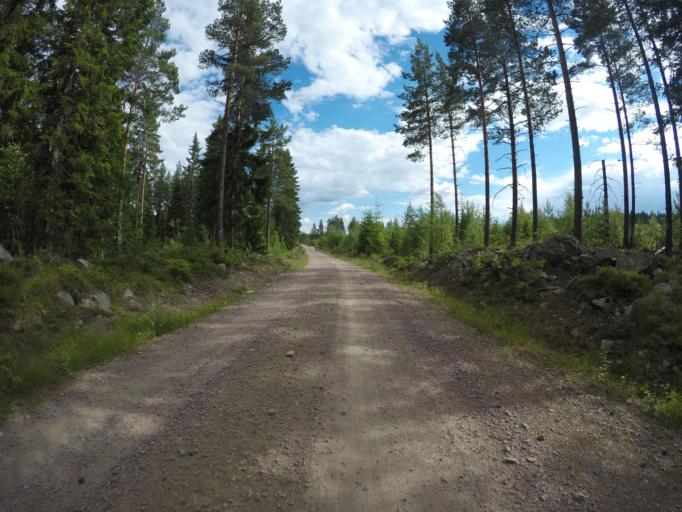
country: SE
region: Vaermland
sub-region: Filipstads Kommun
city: Lesjofors
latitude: 60.0766
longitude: 14.4253
